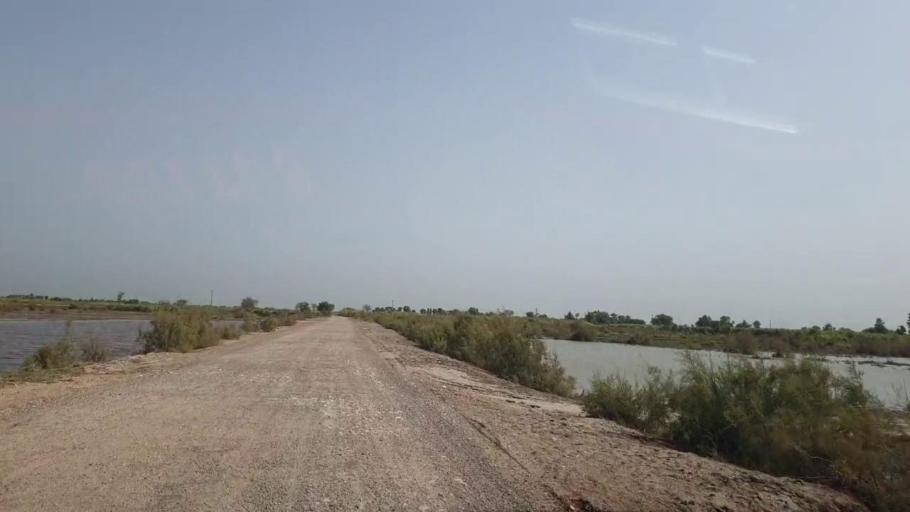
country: PK
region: Sindh
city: Sakrand
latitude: 26.3030
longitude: 68.2204
